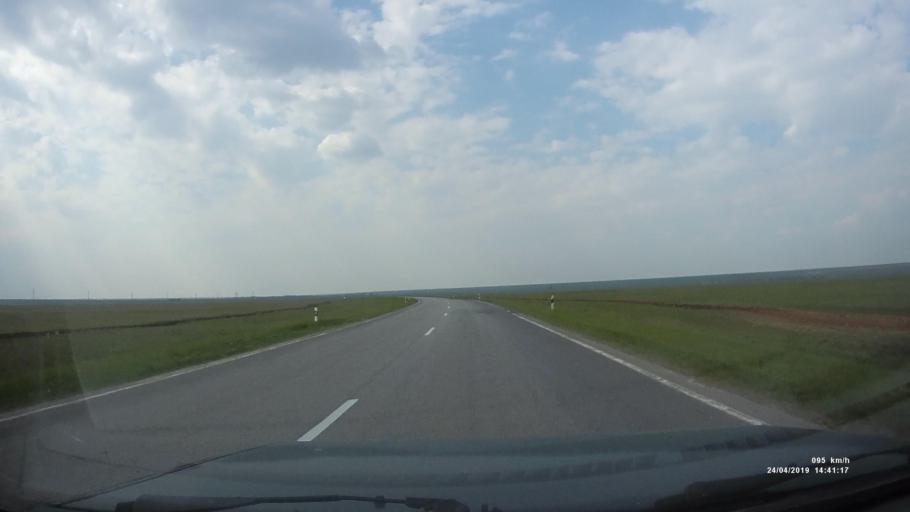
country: RU
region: Rostov
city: Remontnoye
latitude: 46.4435
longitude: 43.8817
